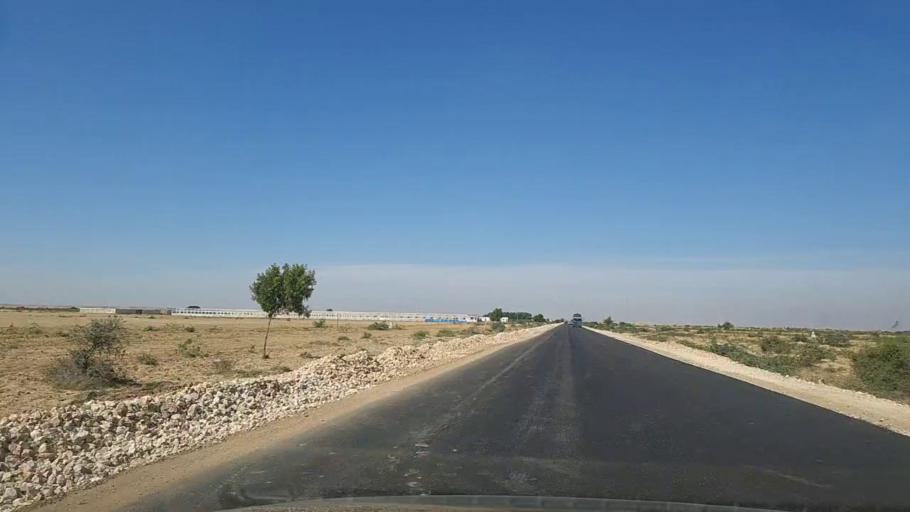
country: PK
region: Sindh
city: Kotri
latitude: 25.2542
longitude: 68.2259
